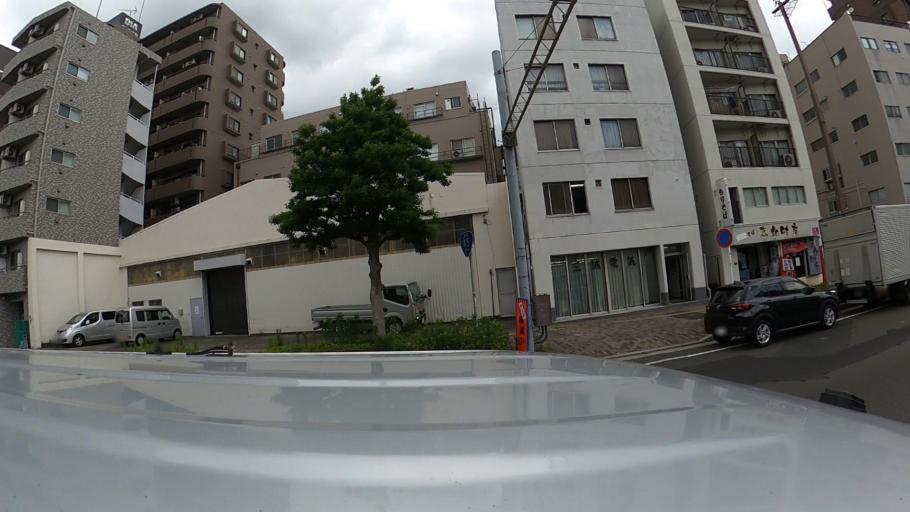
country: JP
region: Kanagawa
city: Yokohama
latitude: 35.4771
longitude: 139.6368
